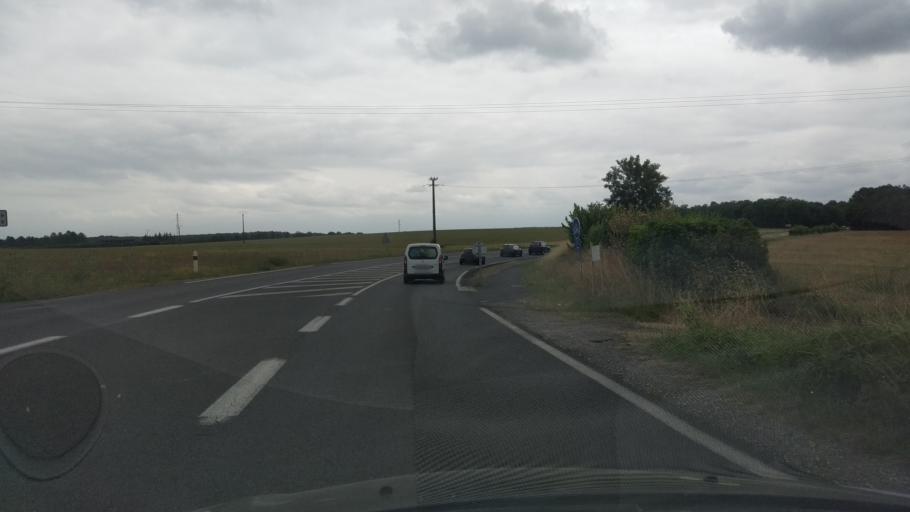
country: FR
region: Poitou-Charentes
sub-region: Departement de la Vienne
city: Saint-Benoit
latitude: 46.5410
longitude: 0.3544
